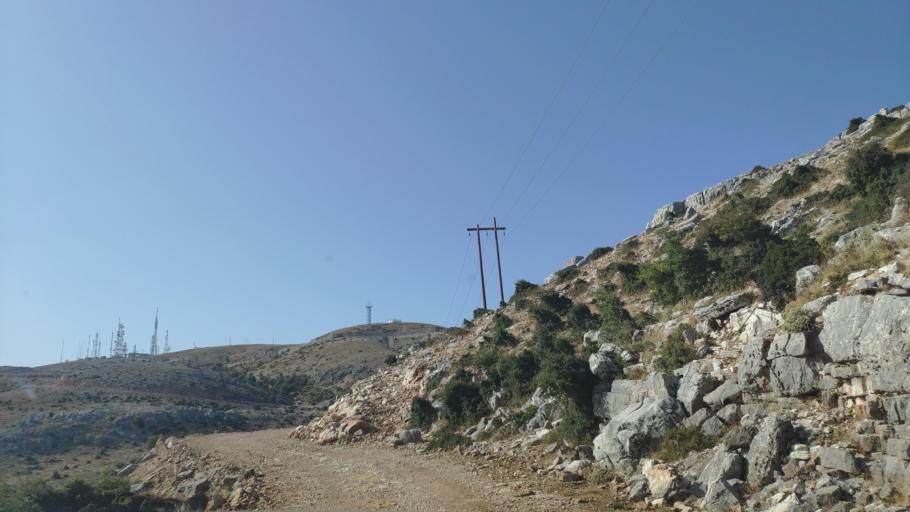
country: GR
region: West Greece
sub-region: Nomos Aitolias kai Akarnanias
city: Monastirakion
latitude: 38.8162
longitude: 20.9790
